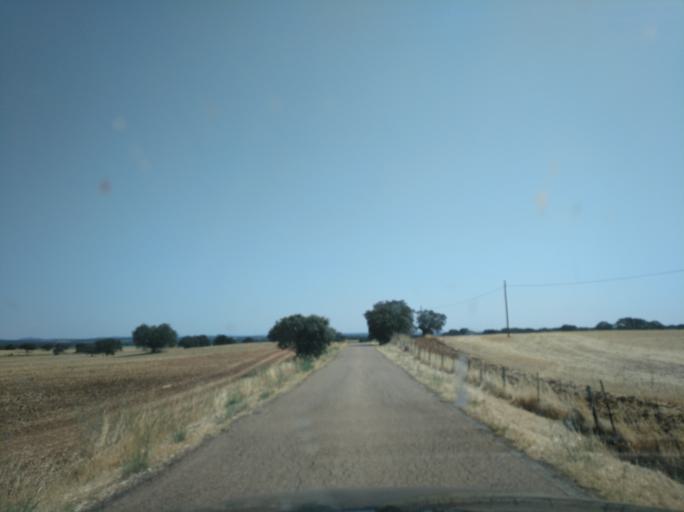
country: PT
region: Portalegre
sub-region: Campo Maior
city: Campo Maior
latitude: 39.0329
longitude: -6.9966
